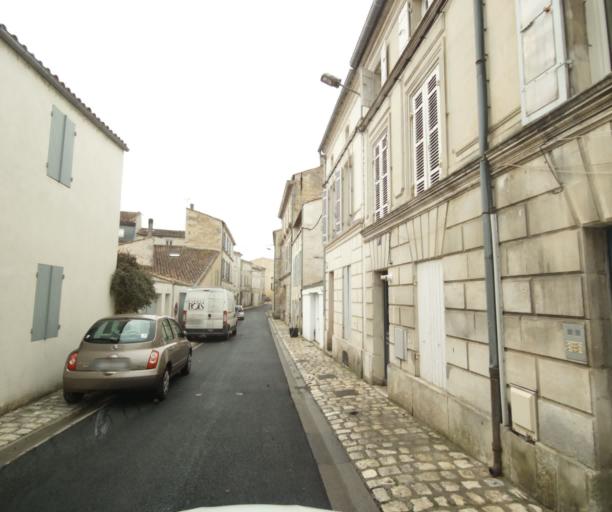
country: FR
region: Poitou-Charentes
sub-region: Departement de la Charente-Maritime
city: Saintes
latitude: 45.7435
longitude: -0.6377
